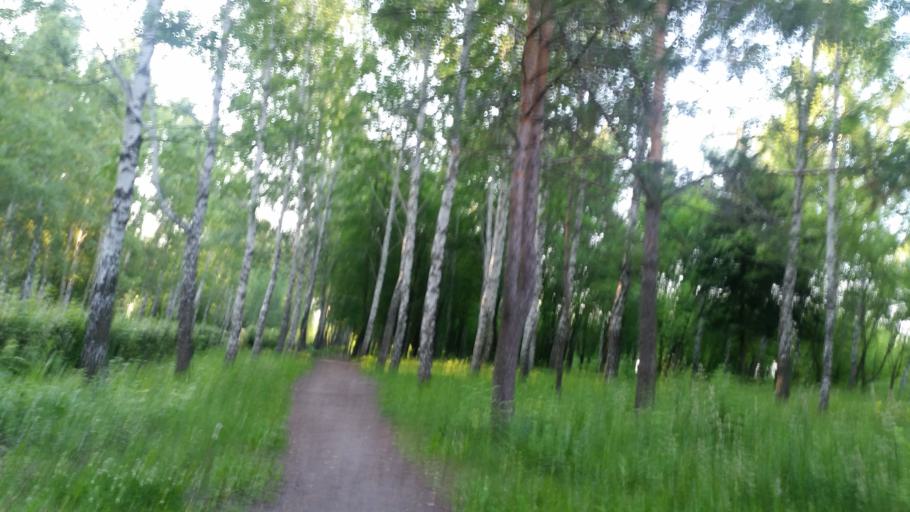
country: RU
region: Ulyanovsk
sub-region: Ulyanovskiy Rayon
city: Ulyanovsk
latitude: 54.3480
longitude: 48.3942
